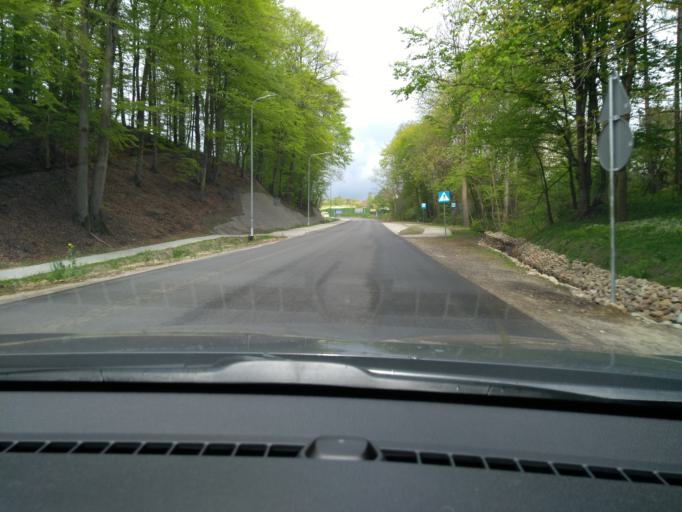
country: PL
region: Pomeranian Voivodeship
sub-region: Powiat kartuski
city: Sierakowice
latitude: 54.3390
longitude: 17.9732
